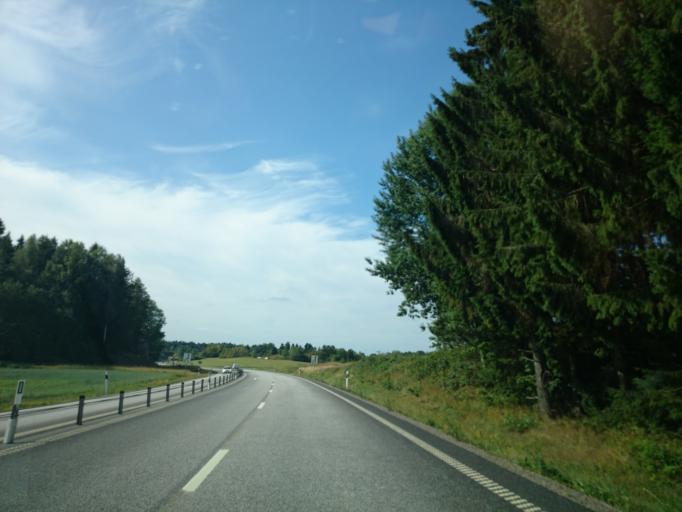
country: SE
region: Kalmar
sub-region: Vasterviks Kommun
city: Forserum
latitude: 57.9583
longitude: 16.4432
